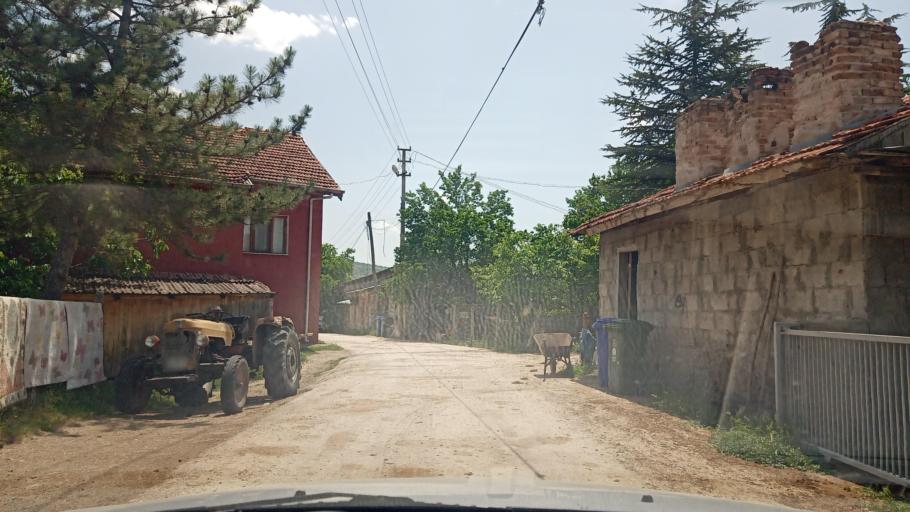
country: TR
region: Bolu
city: Seben
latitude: 40.4136
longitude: 31.5792
